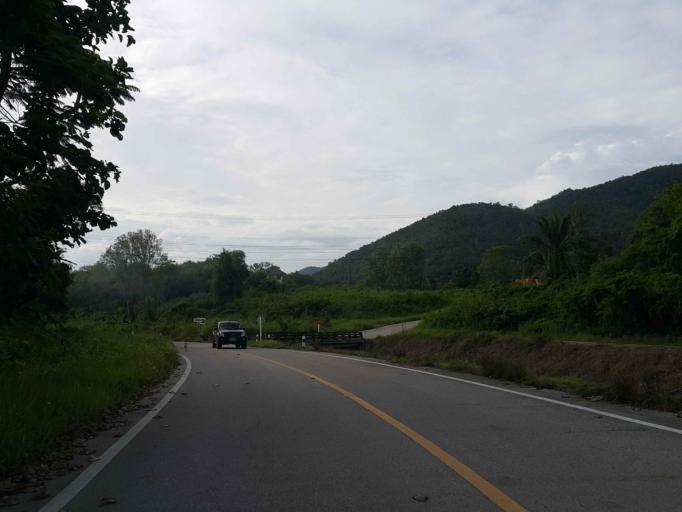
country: TH
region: Chiang Mai
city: San Sai
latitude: 18.9331
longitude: 99.1422
